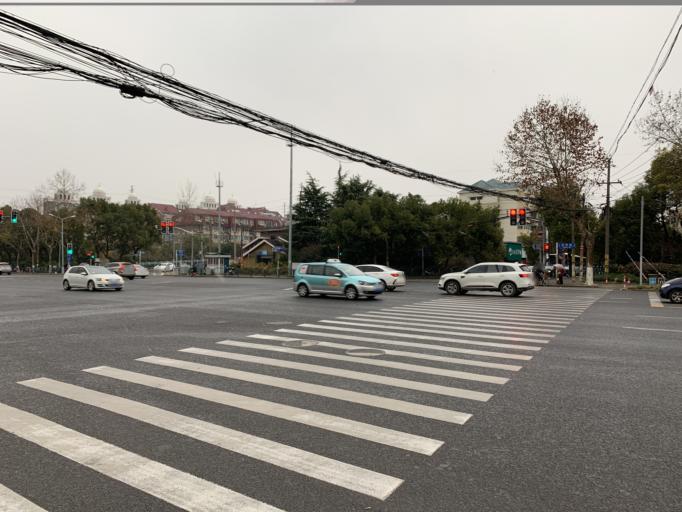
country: CN
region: Shanghai Shi
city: Huamu
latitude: 31.1863
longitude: 121.5364
